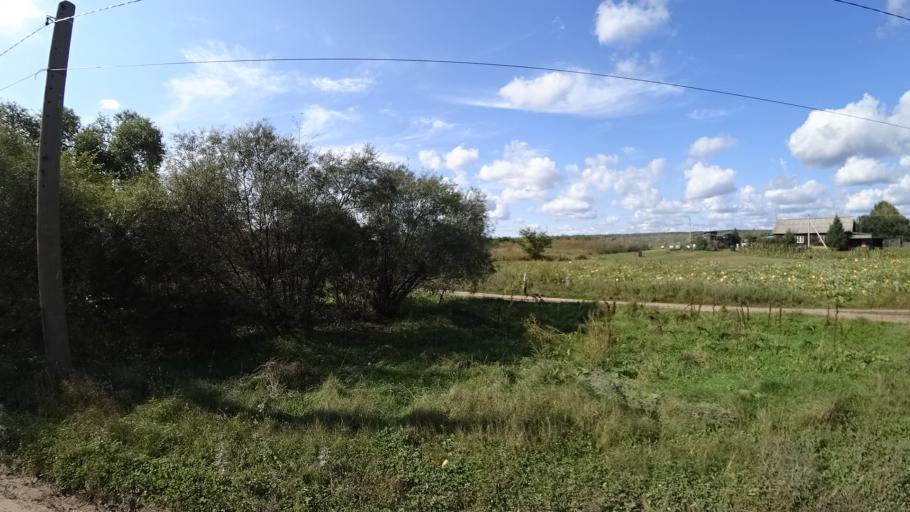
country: RU
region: Amur
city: Arkhara
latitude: 49.4031
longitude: 130.1523
